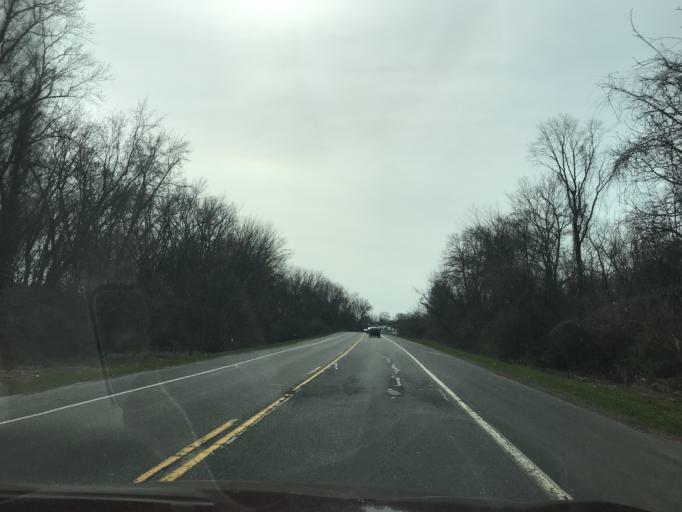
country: US
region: Pennsylvania
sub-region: Union County
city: Lewisburg
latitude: 40.9678
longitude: -76.8711
